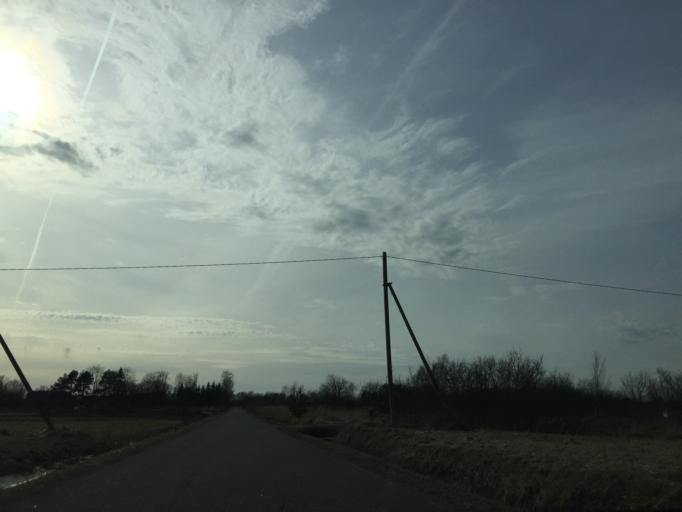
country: EE
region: Paernumaa
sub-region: Paernu linn
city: Parnu
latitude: 58.2463
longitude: 24.4963
